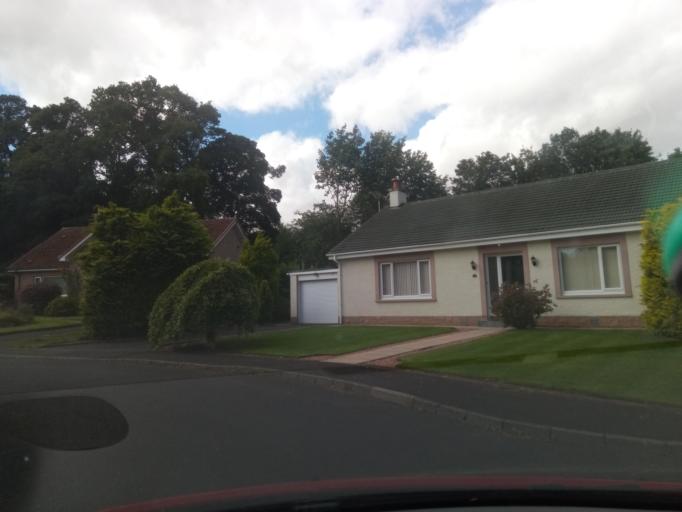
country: GB
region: Scotland
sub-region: The Scottish Borders
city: Coldstream
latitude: 55.6497
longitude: -2.2603
